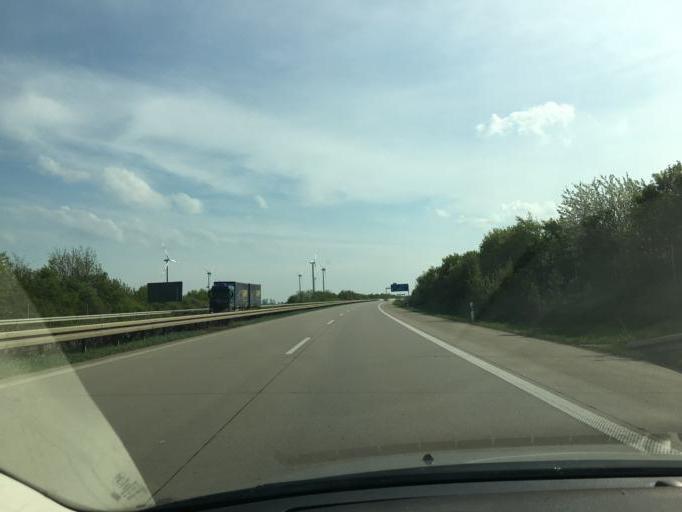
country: DE
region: Saxony-Anhalt
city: Dahlenwarsleben
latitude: 52.1896
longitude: 11.5512
